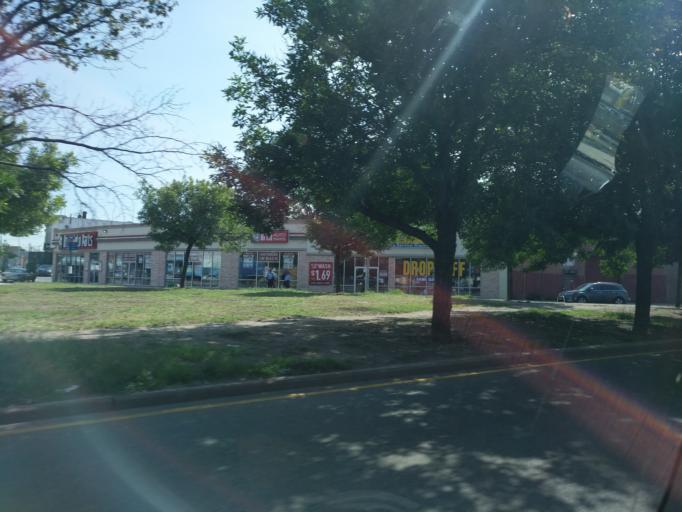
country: US
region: New York
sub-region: Queens County
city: Jamaica
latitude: 40.7021
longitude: -73.7909
